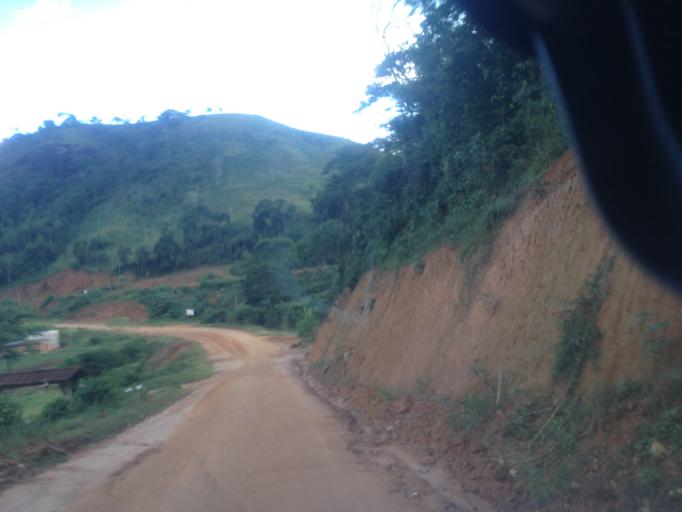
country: BR
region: Rio de Janeiro
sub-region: Quatis
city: Quatis
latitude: -22.2386
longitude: -44.2623
